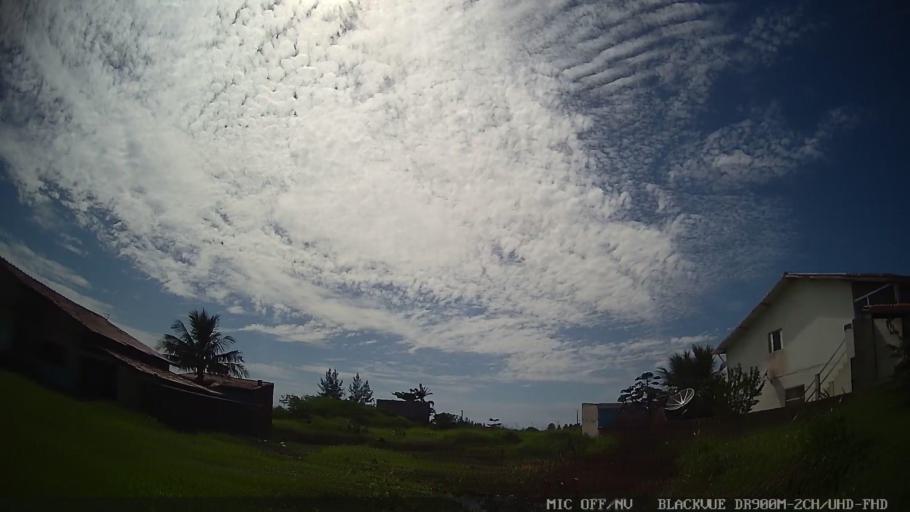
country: BR
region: Sao Paulo
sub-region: Iguape
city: Iguape
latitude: -24.7898
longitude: -47.6181
